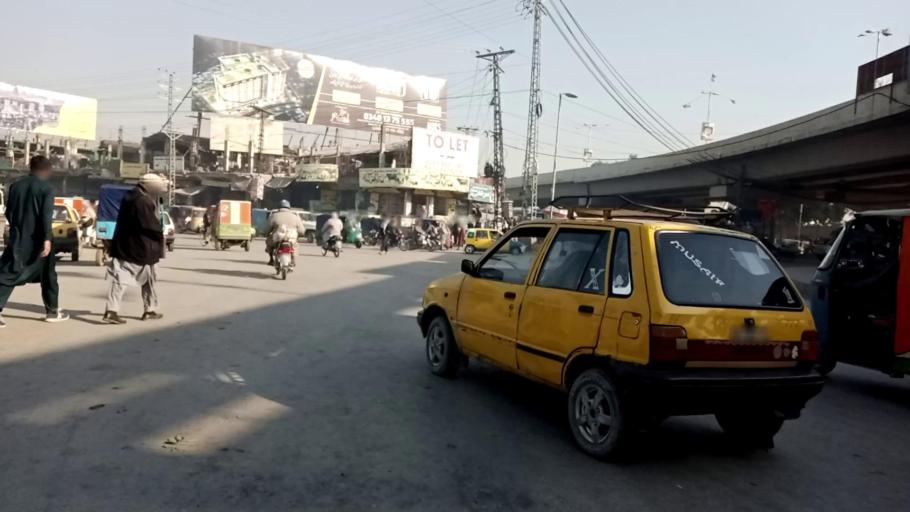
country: PK
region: Khyber Pakhtunkhwa
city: Peshawar
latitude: 34.0172
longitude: 71.5708
